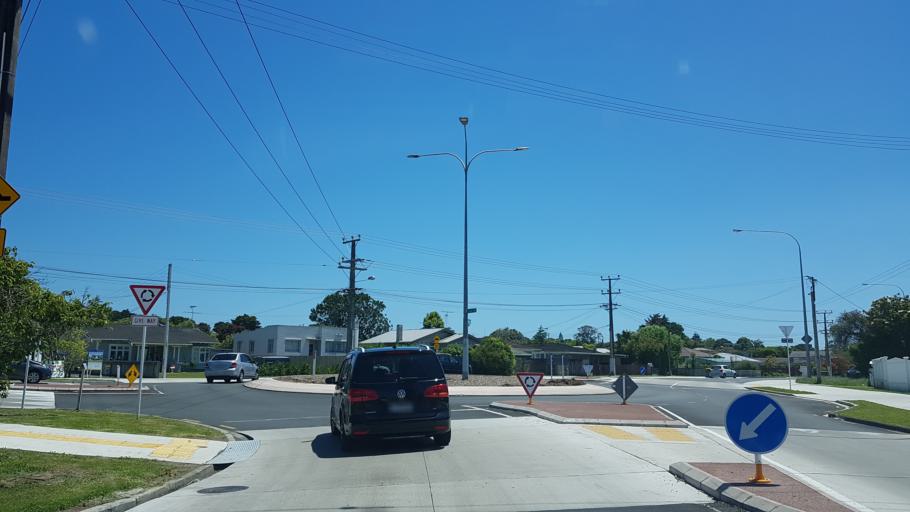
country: NZ
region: Auckland
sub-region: Auckland
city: North Shore
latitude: -36.7946
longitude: 174.7454
